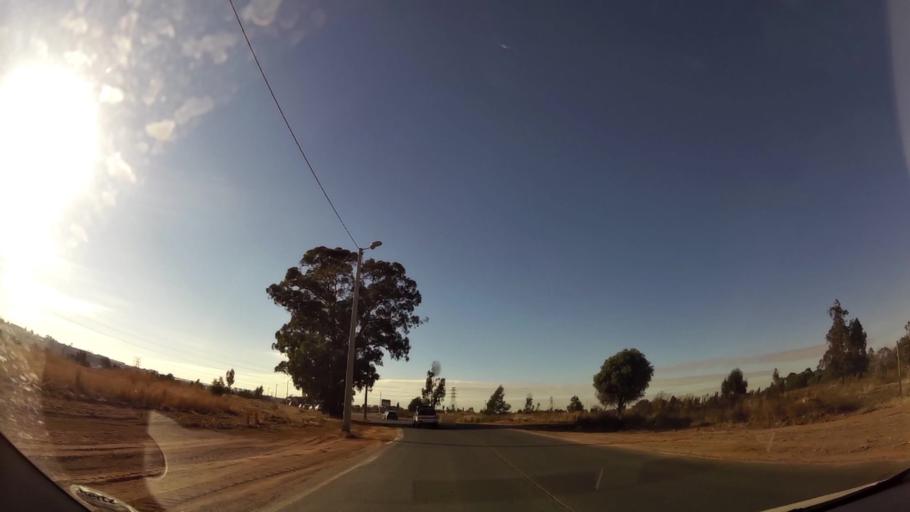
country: ZA
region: Gauteng
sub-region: West Rand District Municipality
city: Krugersdorp
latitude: -26.1194
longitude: 27.7983
